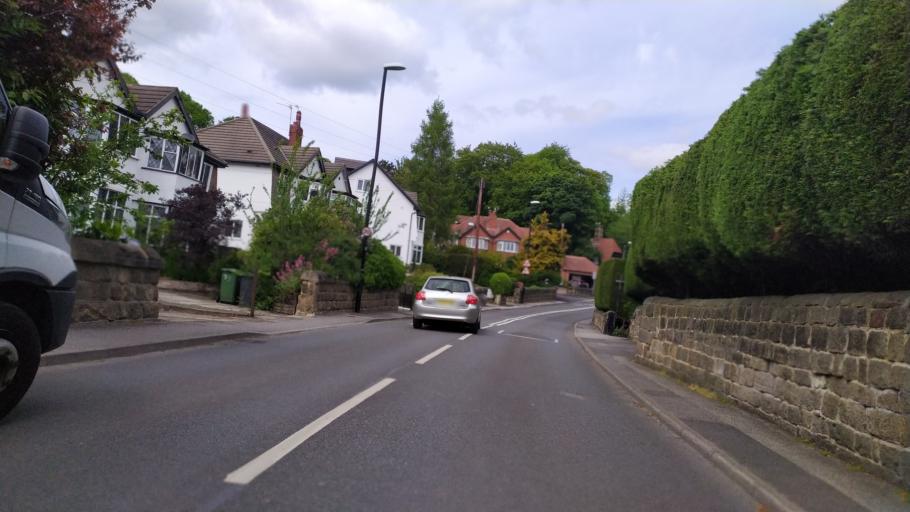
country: GB
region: England
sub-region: City and Borough of Leeds
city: Chapel Allerton
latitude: 53.8336
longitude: -1.5834
